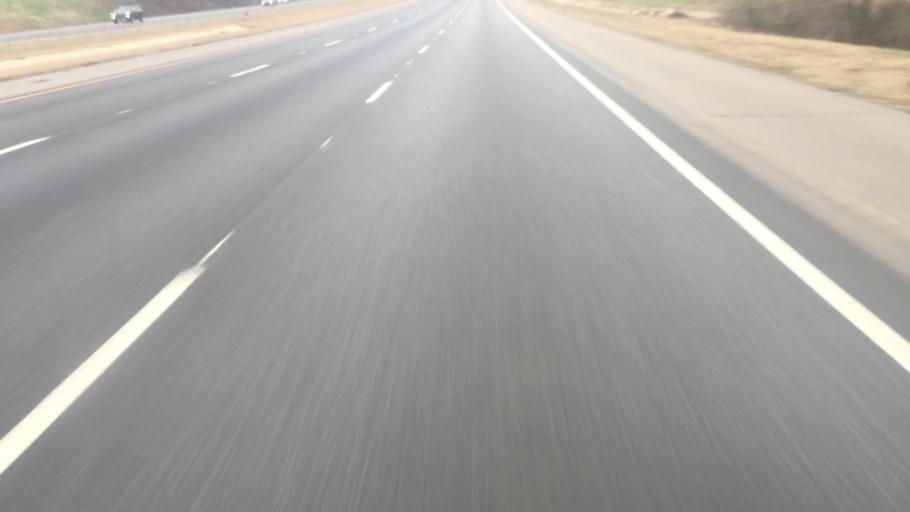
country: US
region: Alabama
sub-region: Jefferson County
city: Forestdale
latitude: 33.5880
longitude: -86.8464
